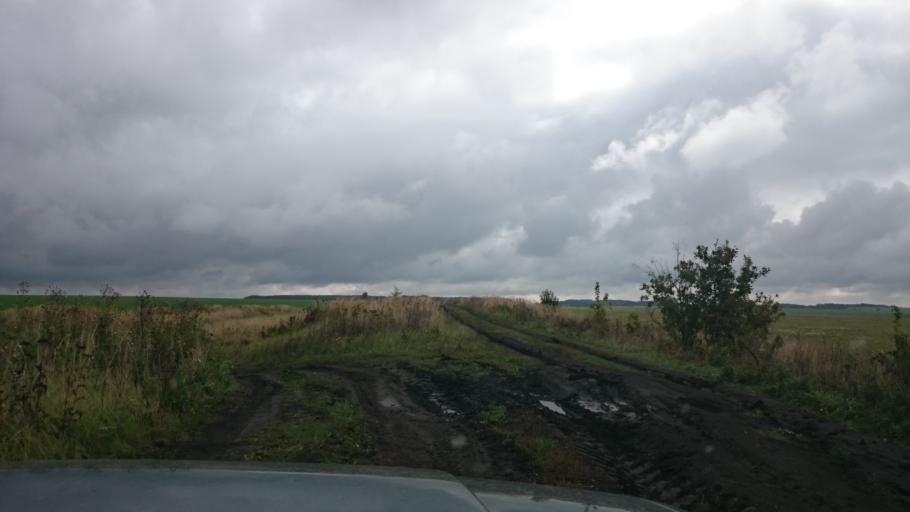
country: RU
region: Mordoviya
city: Kadoshkino
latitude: 54.0157
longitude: 44.4635
